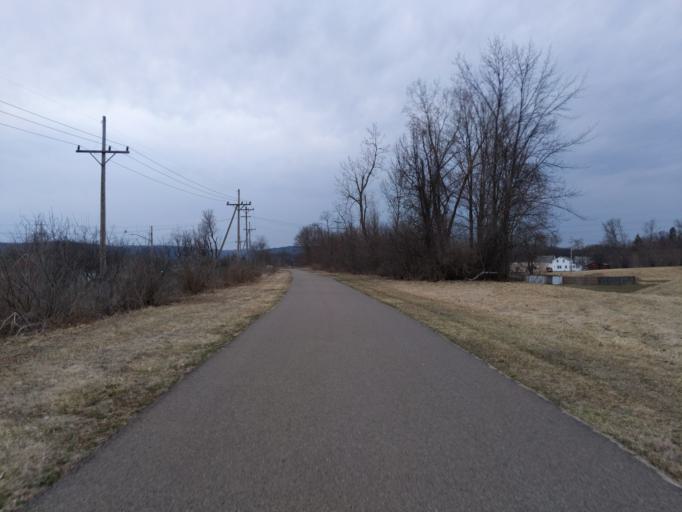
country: US
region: New York
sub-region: Chemung County
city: Elmira
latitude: 42.0973
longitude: -76.7944
